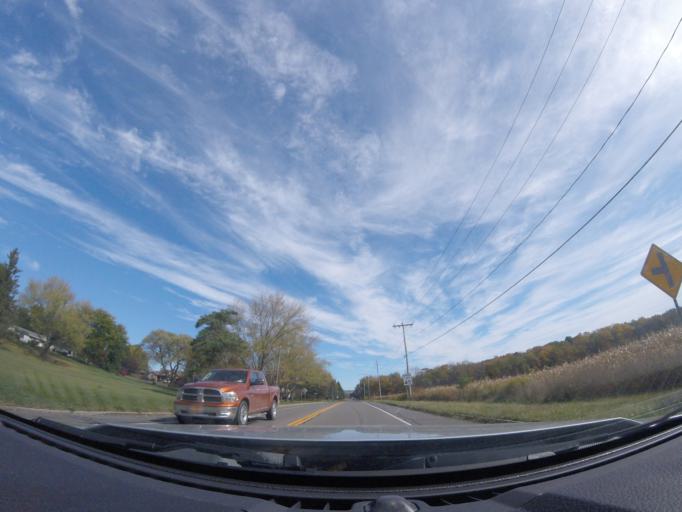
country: US
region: New York
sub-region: Cortland County
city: Cortland West
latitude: 42.5746
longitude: -76.2455
